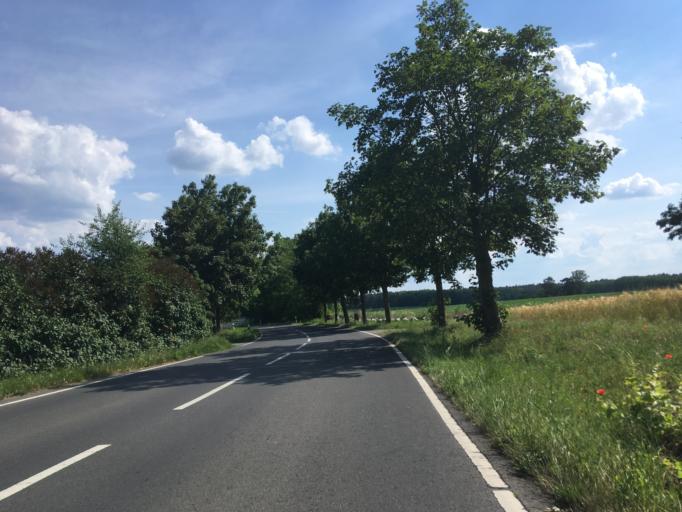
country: DE
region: Brandenburg
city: Steinhofel
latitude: 52.4380
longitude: 14.1007
